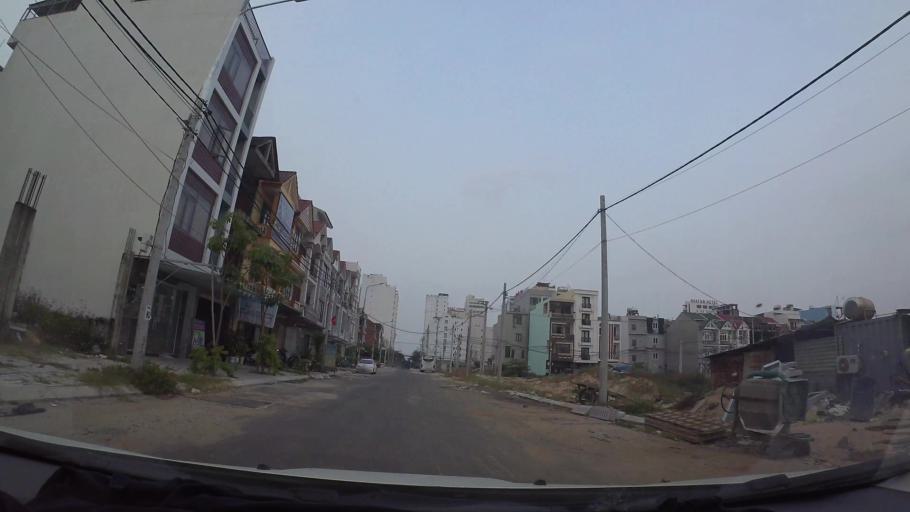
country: VN
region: Da Nang
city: Son Tra
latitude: 16.0509
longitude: 108.2435
